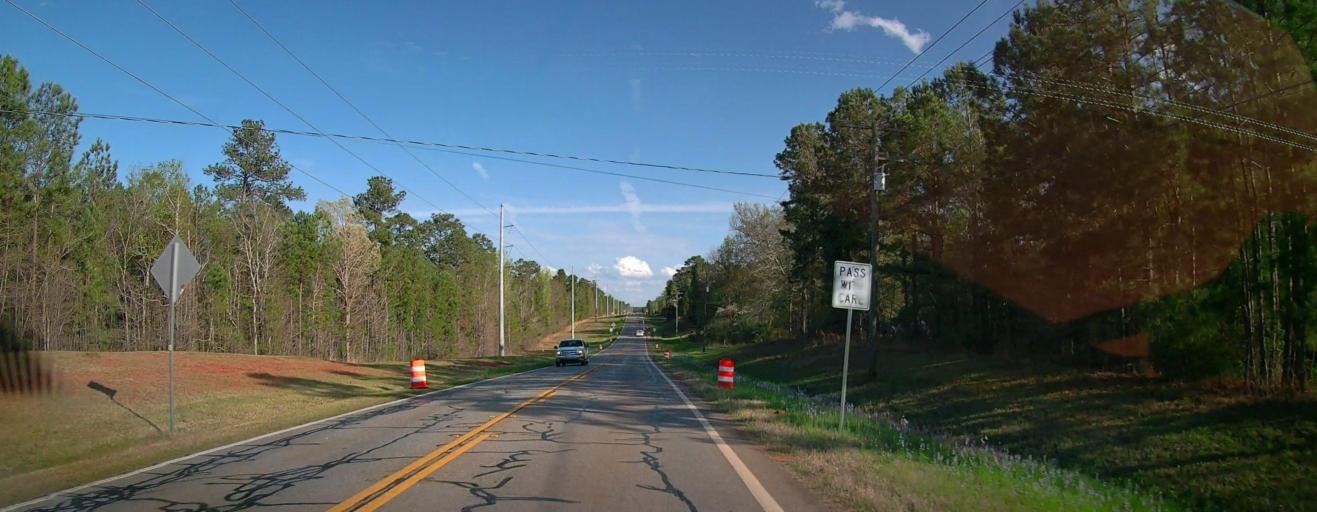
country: US
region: Georgia
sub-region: Baldwin County
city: Milledgeville
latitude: 33.1405
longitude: -83.3314
